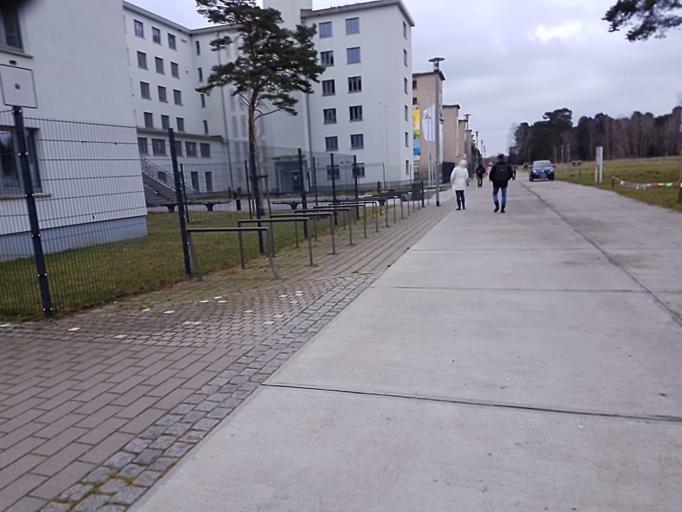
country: DE
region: Mecklenburg-Vorpommern
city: Ostseebad Binz
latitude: 54.4511
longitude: 13.5694
